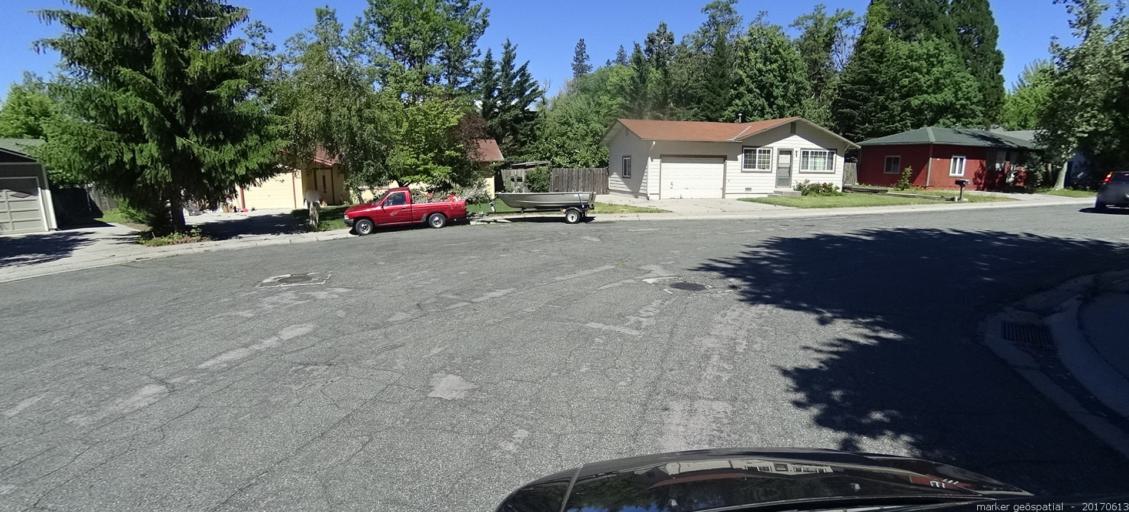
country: US
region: California
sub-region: Siskiyou County
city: Mount Shasta
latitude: 41.3201
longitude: -122.3153
